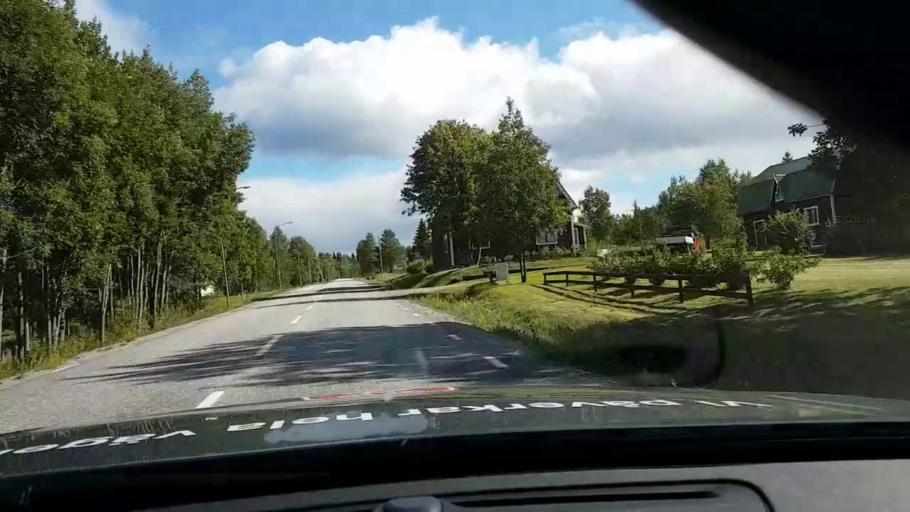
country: SE
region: Vaesterbotten
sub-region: Asele Kommun
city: Asele
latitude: 63.7848
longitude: 17.6531
